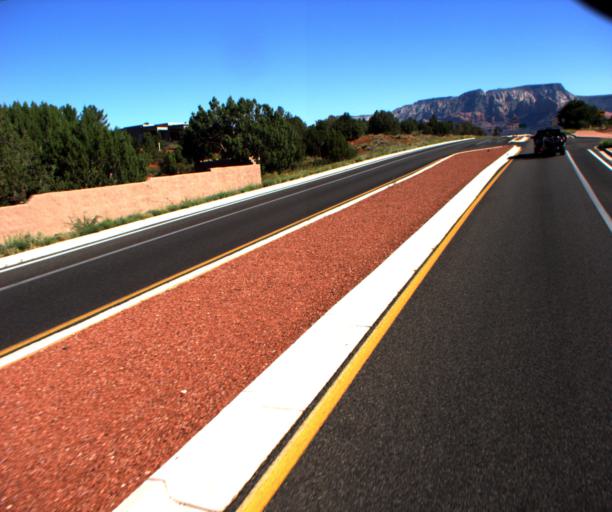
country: US
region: Arizona
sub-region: Coconino County
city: Sedona
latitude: 34.8302
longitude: -111.7777
